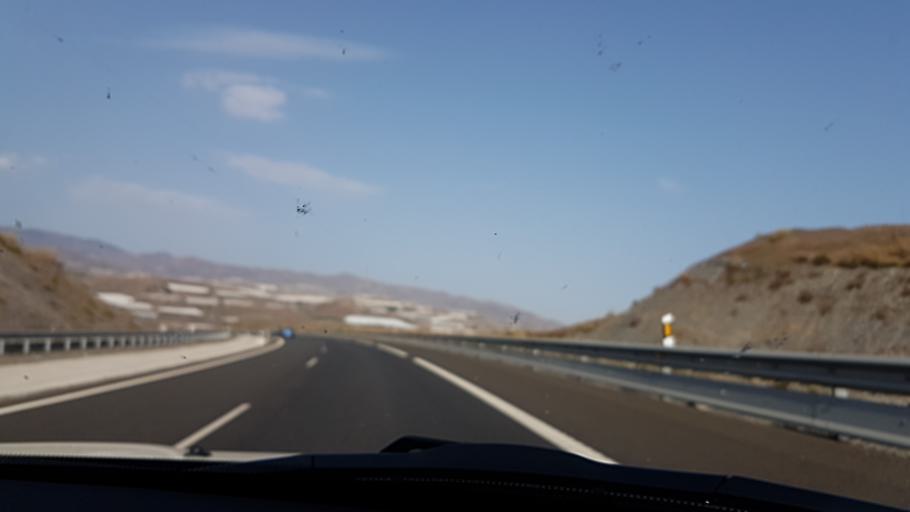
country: ES
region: Andalusia
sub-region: Provincia de Granada
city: Albunol
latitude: 36.7502
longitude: -3.2100
